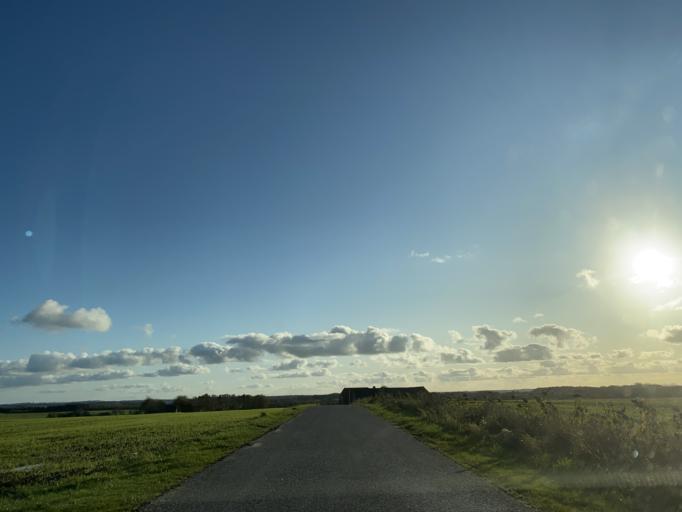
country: DK
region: Central Jutland
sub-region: Viborg Kommune
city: Bjerringbro
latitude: 56.3337
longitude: 9.7097
